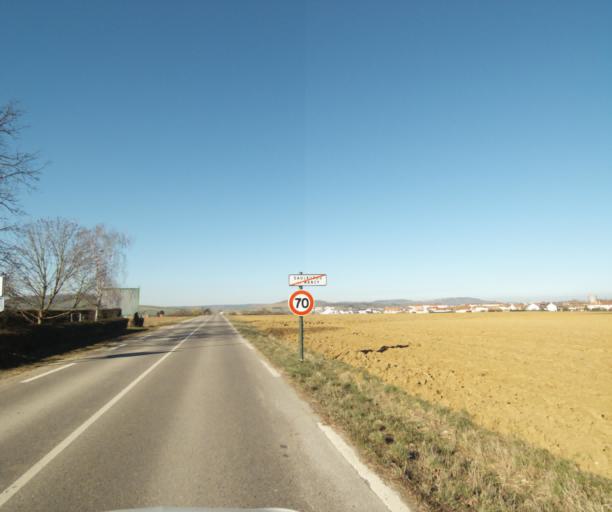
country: FR
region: Lorraine
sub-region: Departement de Meurthe-et-Moselle
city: Saulxures-les-Nancy
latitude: 48.6941
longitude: 6.2505
